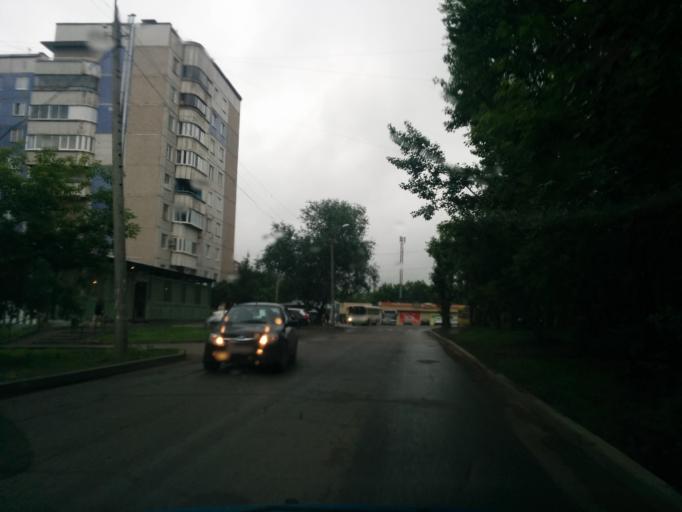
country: RU
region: Perm
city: Perm
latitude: 57.9905
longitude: 56.2329
